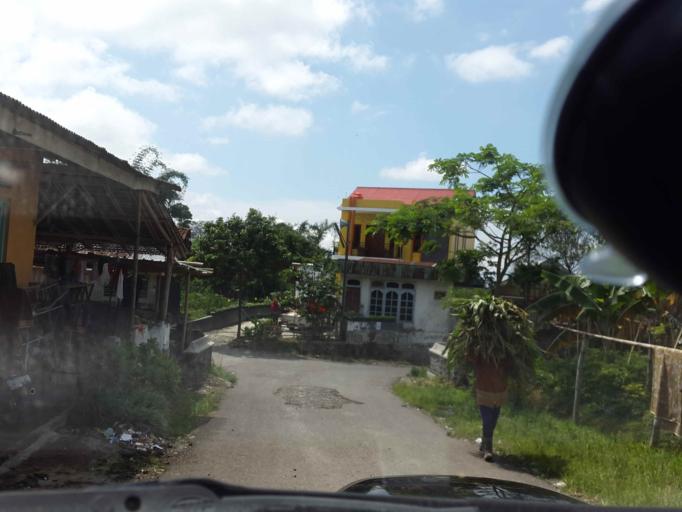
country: ID
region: Central Java
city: Wonosobo
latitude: -7.3873
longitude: 109.9945
